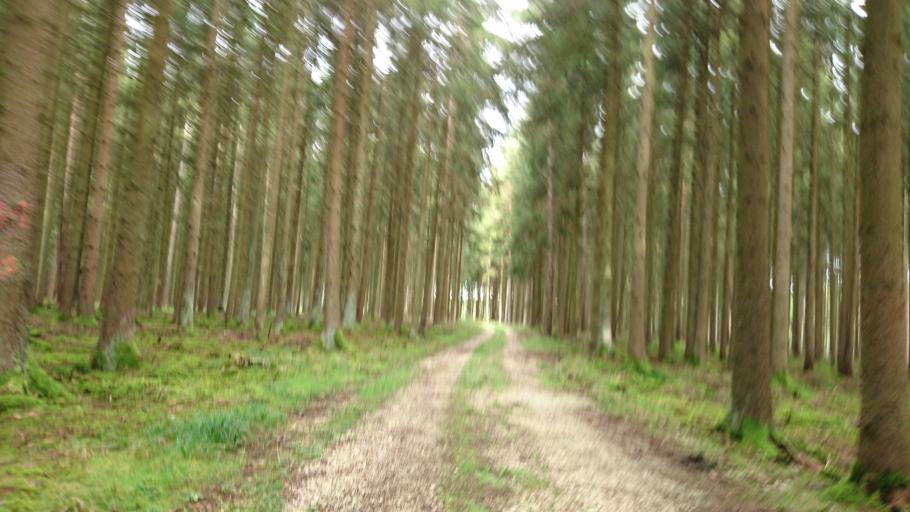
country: DE
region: Bavaria
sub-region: Swabia
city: Welden
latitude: 48.4370
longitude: 10.6387
